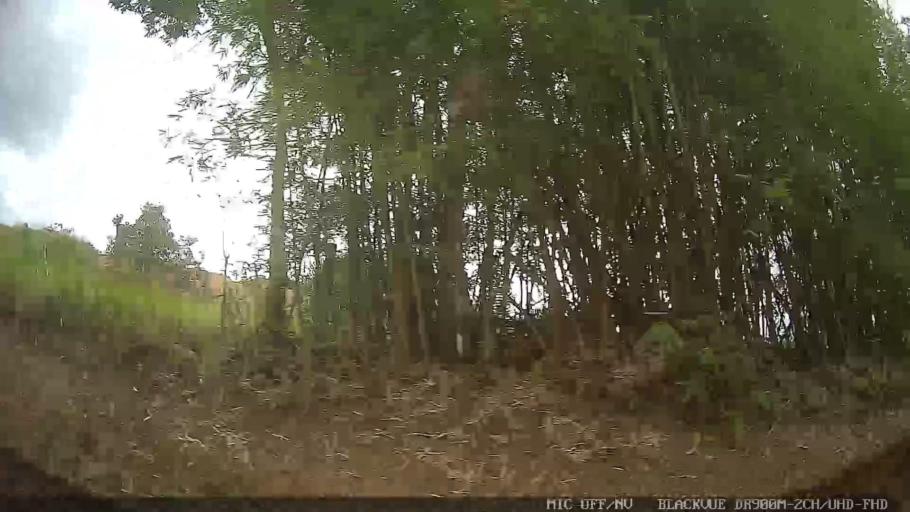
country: BR
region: Sao Paulo
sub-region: Aruja
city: Aruja
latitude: -23.4250
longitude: -46.2295
